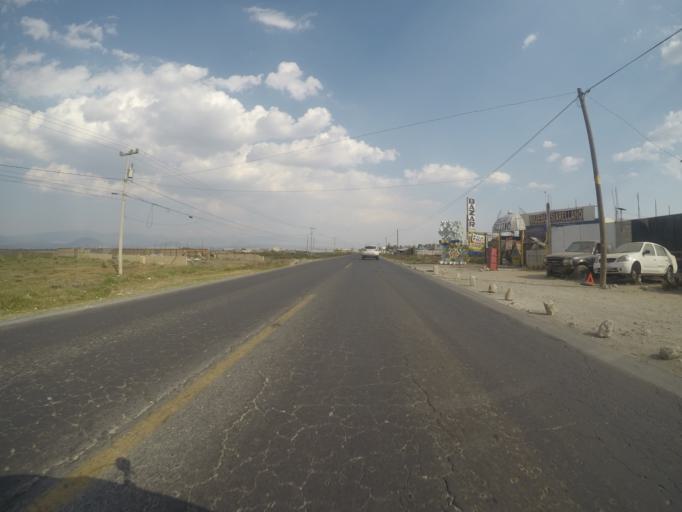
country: MX
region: Morelos
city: Chapultepec
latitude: 19.1971
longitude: -99.5430
